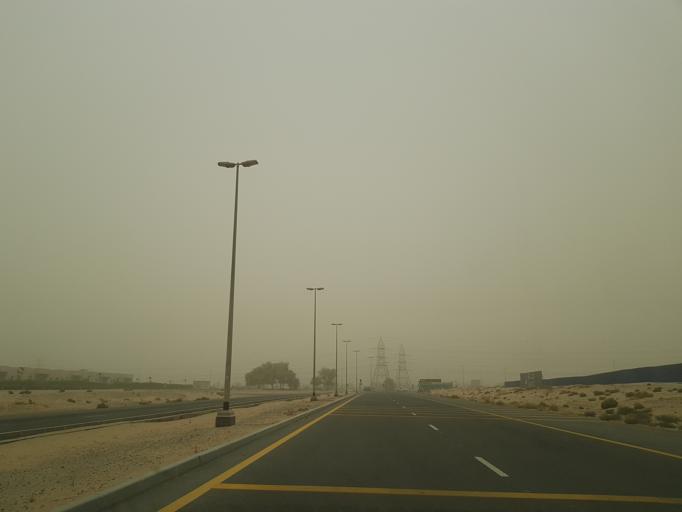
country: AE
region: Dubai
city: Dubai
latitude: 25.1427
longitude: 55.2885
